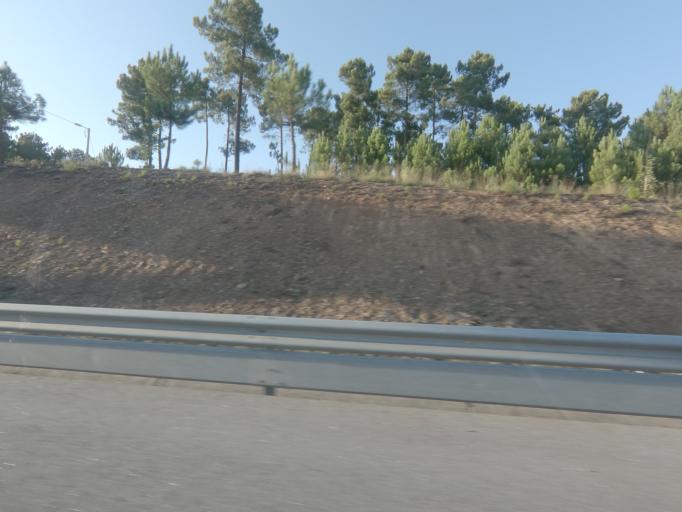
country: PT
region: Vila Real
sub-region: Vila Real
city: Vila Real
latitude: 41.2711
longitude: -7.6906
